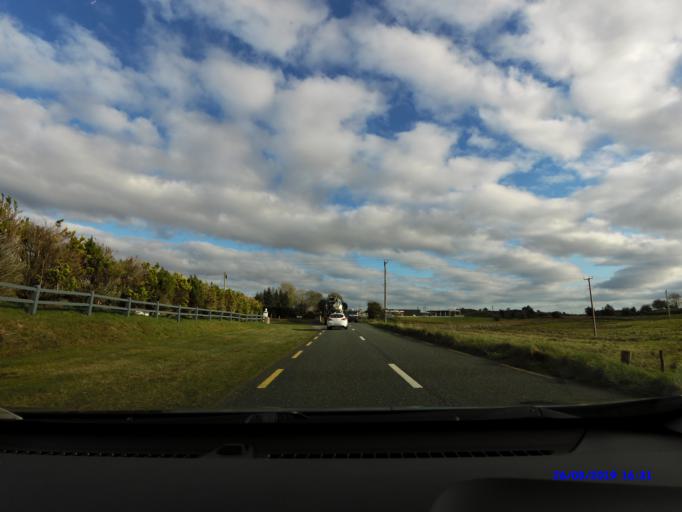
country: IE
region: Connaught
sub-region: Maigh Eo
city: Swinford
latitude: 53.8769
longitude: -8.8580
